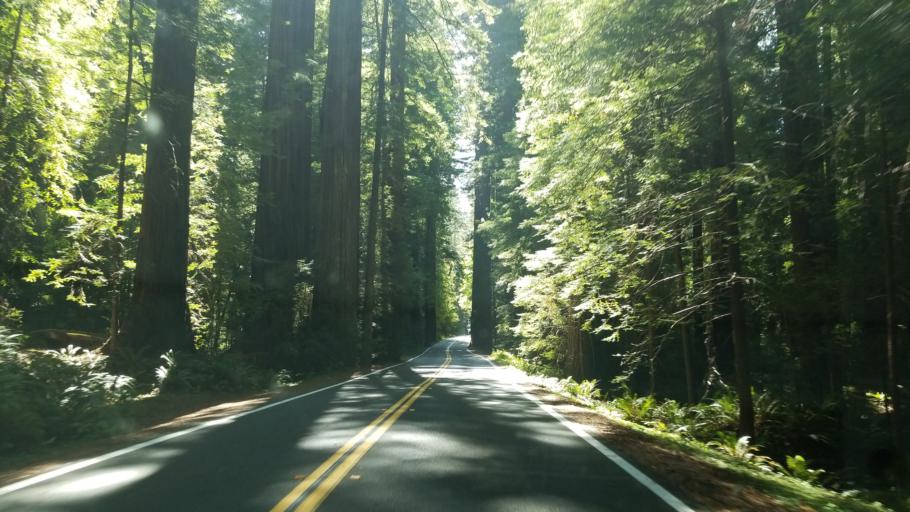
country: US
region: California
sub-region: Humboldt County
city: Rio Dell
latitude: 40.3432
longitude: -123.9333
